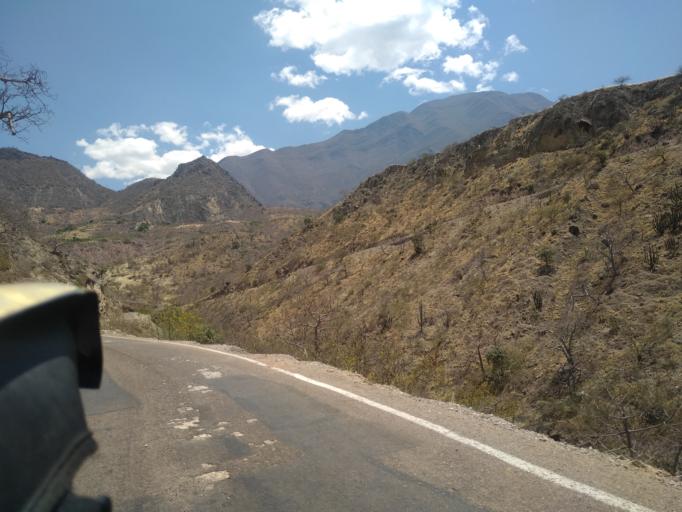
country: PE
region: Amazonas
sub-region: Provincia de Chachapoyas
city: Balsas
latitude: -6.8514
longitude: -78.0377
